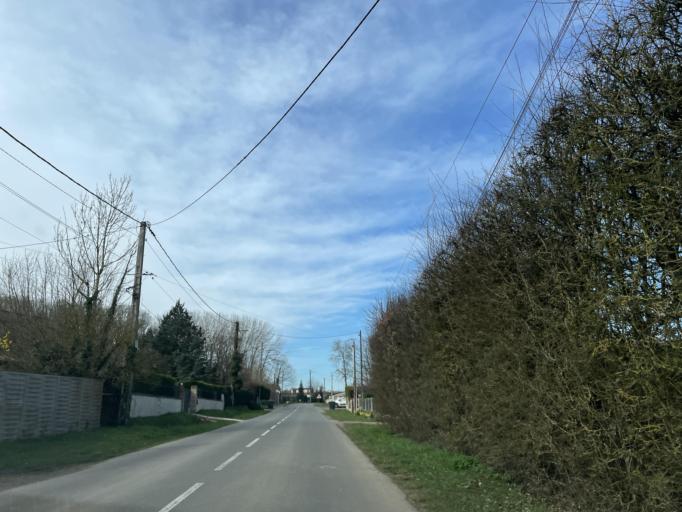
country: FR
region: Ile-de-France
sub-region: Departement de Seine-et-Marne
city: Chailly-en-Brie
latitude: 48.7403
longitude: 3.1198
